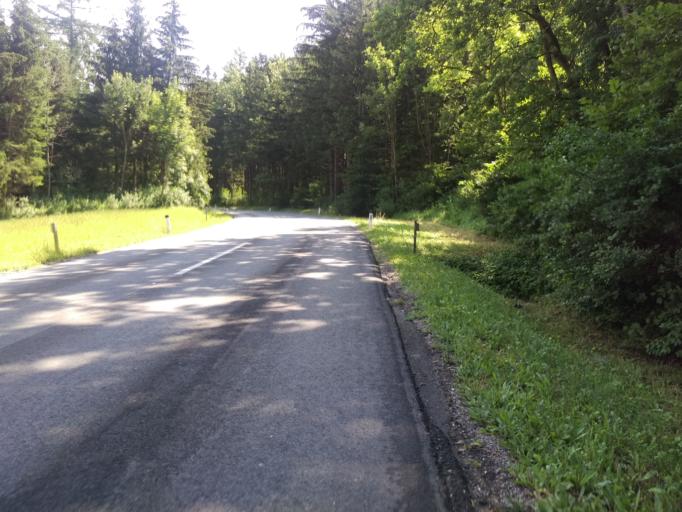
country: AT
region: Styria
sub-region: Politischer Bezirk Graz-Umgebung
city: Sankt Radegund bei Graz
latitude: 47.1382
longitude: 15.4875
